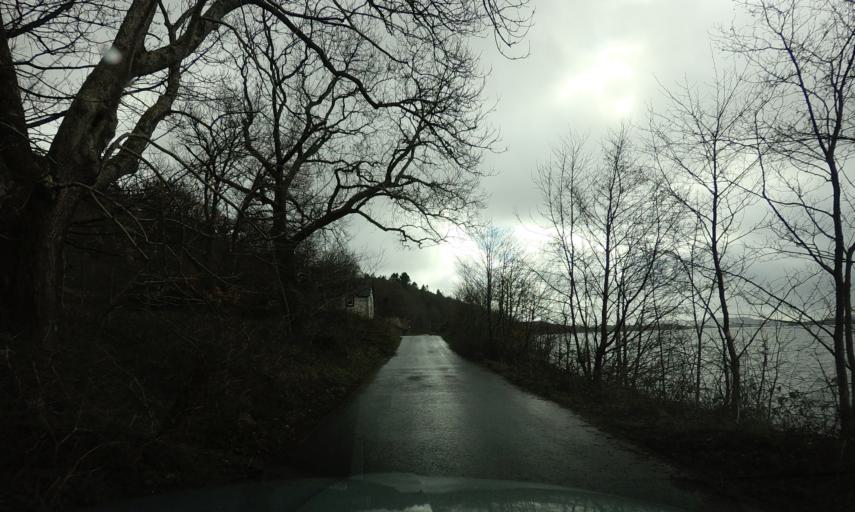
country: GB
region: Scotland
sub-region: West Dunbartonshire
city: Balloch
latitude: 56.1190
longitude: -4.5897
